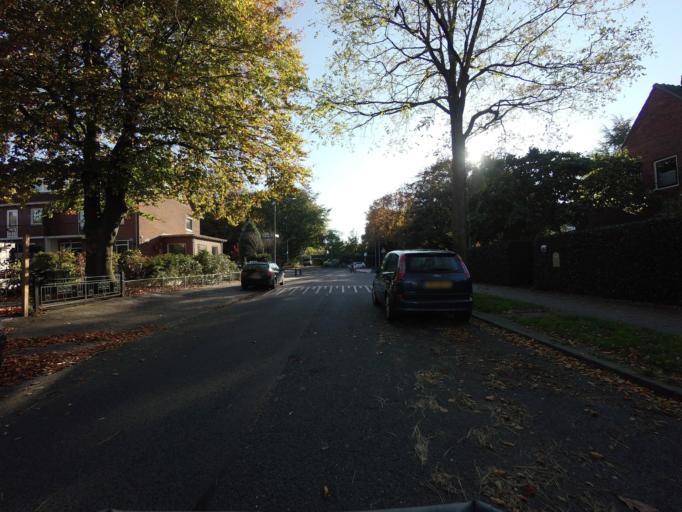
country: NL
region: North Holland
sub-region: Gemeente Hilversum
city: Hilversum
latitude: 52.2084
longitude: 5.1667
